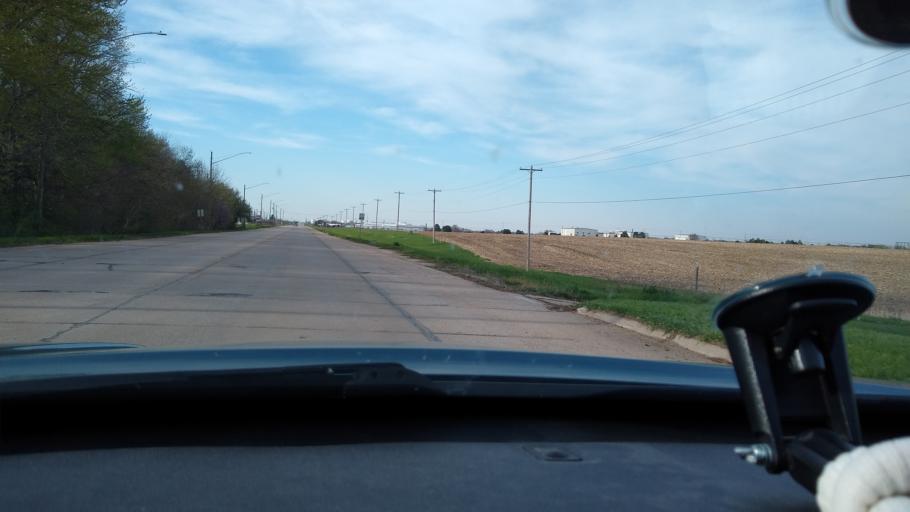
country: US
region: Nebraska
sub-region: Fillmore County
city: Geneva
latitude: 40.5334
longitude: -97.5958
